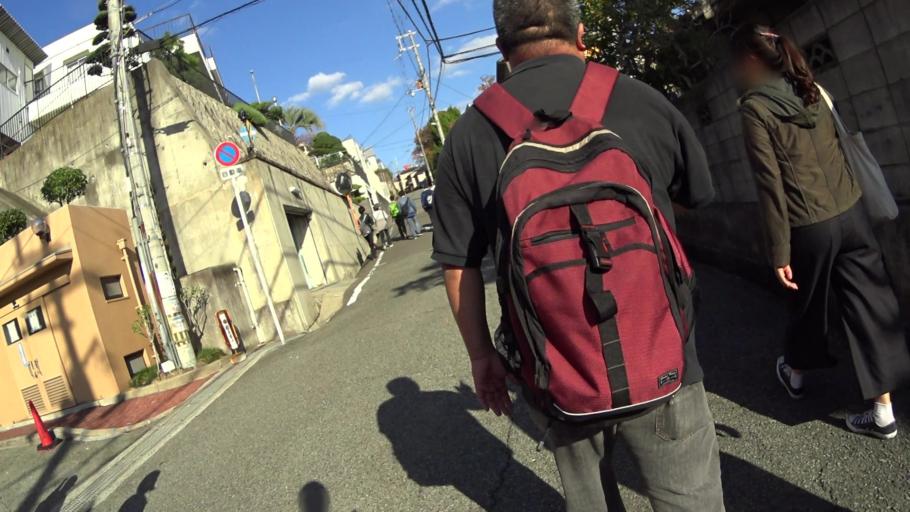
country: JP
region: Osaka
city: Ikeda
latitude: 34.8263
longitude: 135.4327
